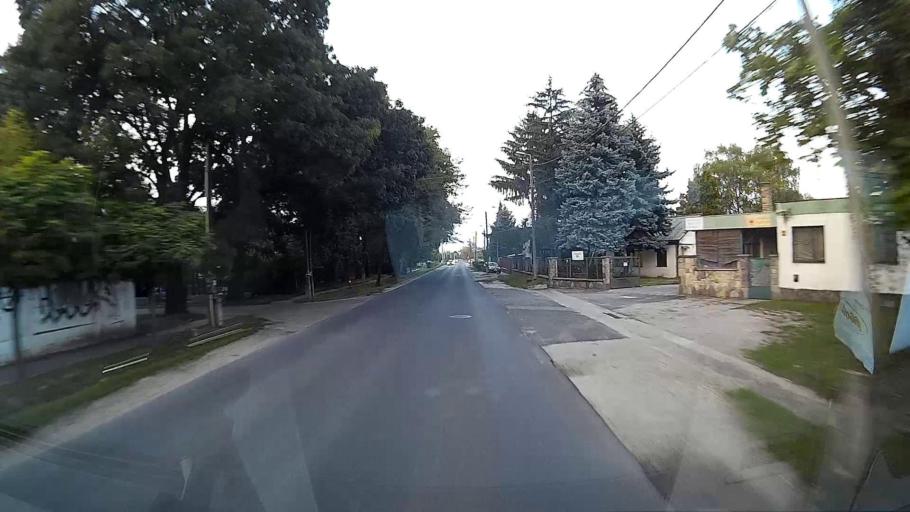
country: HU
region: Pest
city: Budakalasz
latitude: 47.6235
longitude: 19.0509
